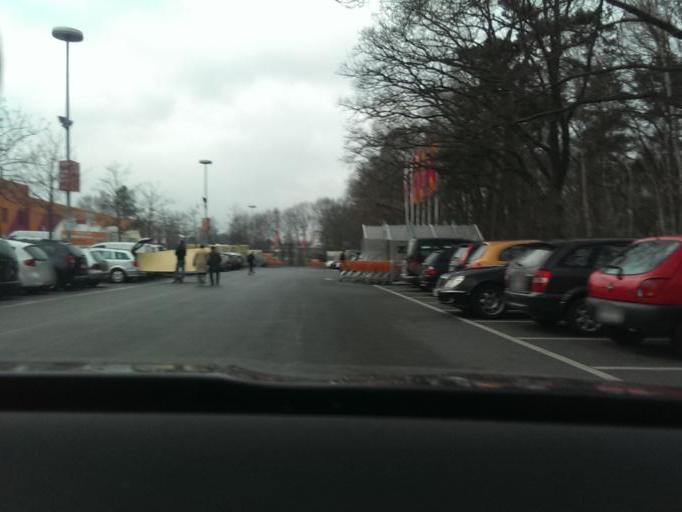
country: DE
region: Lower Saxony
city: Isernhagen Farster Bauerschaft
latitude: 52.4273
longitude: 9.8462
